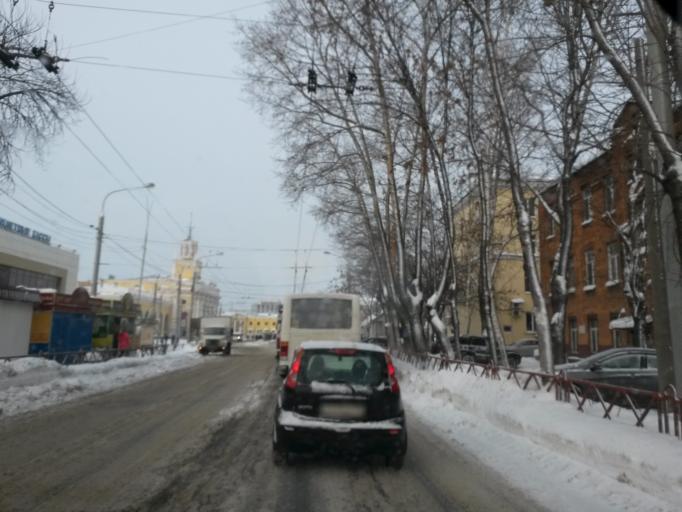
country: RU
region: Jaroslavl
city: Yaroslavl
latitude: 57.6252
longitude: 39.8381
